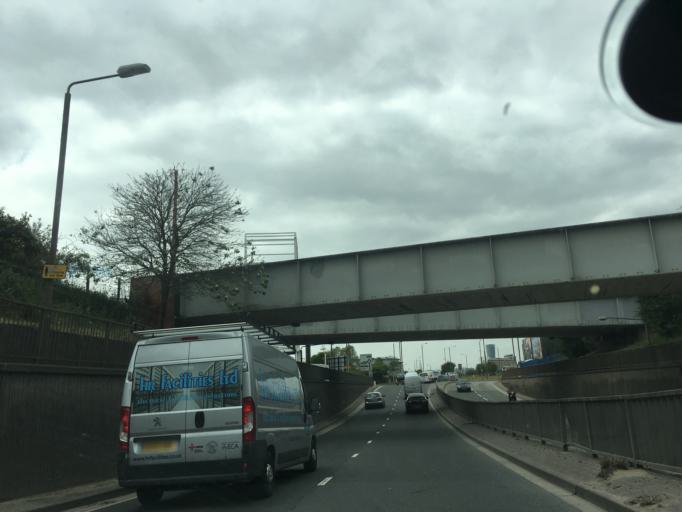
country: GB
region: England
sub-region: Greater London
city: Blackheath
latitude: 51.4900
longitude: 0.0205
